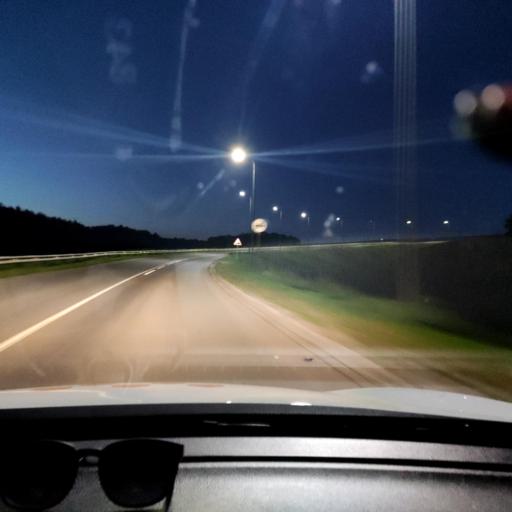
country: RU
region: Tatarstan
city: Rybnaya Sloboda
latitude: 55.4758
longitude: 50.0276
